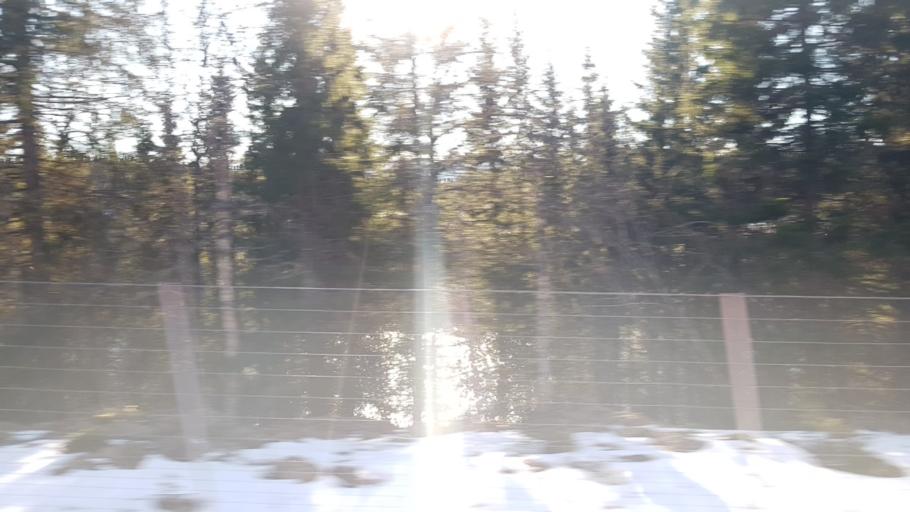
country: NO
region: Nordland
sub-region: Vefsn
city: Mosjoen
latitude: 65.7831
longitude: 13.2164
